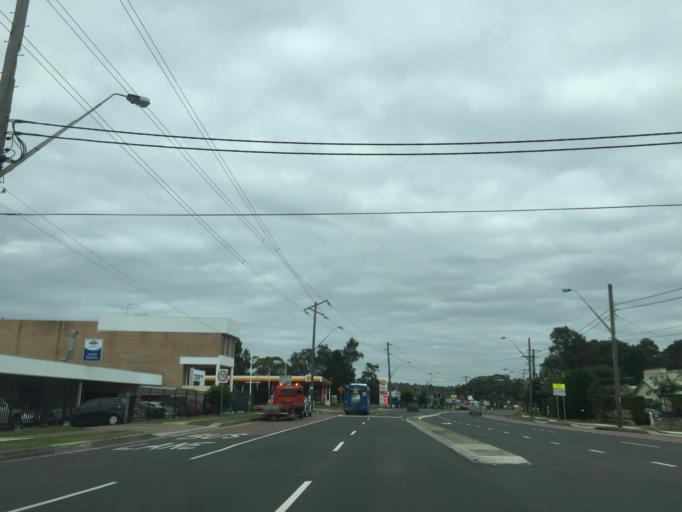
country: AU
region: New South Wales
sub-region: Pittwater
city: North Narrabeen
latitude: -33.6990
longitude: 151.3003
